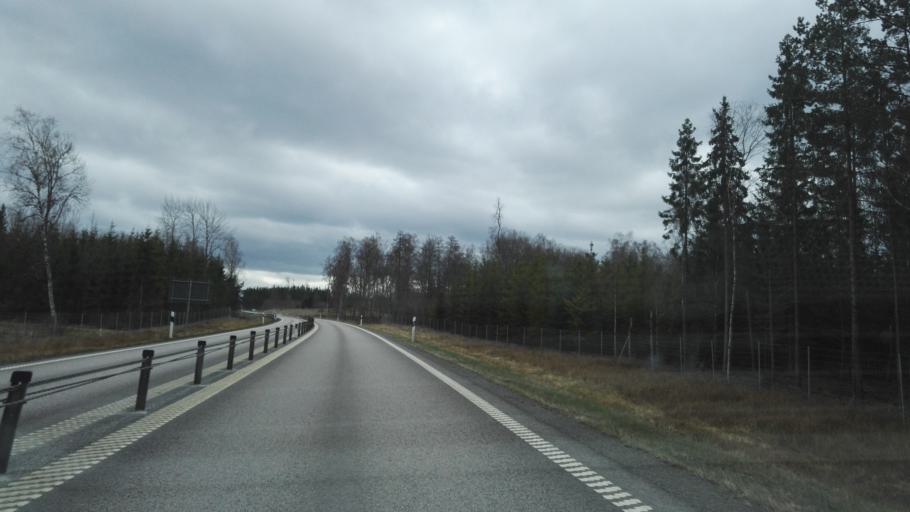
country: SE
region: Kronoberg
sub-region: Alvesta Kommun
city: Vislanda
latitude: 56.6837
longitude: 14.3182
